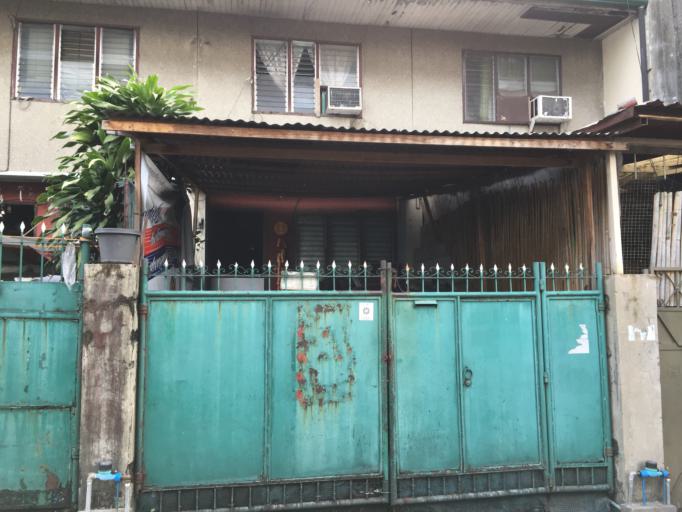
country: PH
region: Metro Manila
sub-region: San Juan
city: San Juan
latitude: 14.6053
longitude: 121.0222
